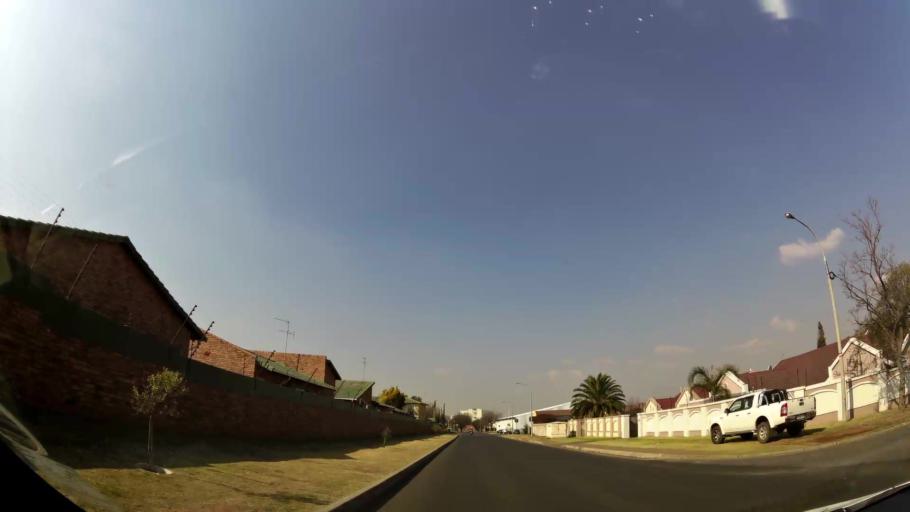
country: ZA
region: Gauteng
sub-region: Ekurhuleni Metropolitan Municipality
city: Boksburg
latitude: -26.1901
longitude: 28.2629
